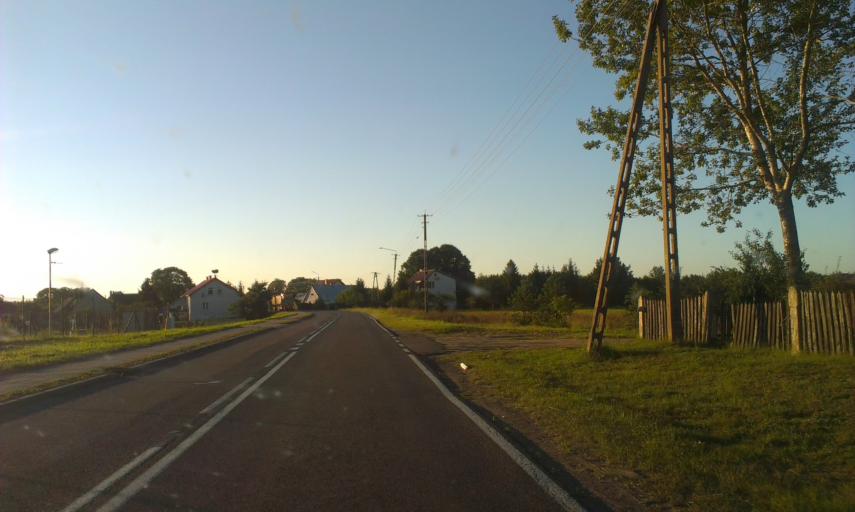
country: PL
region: Pomeranian Voivodeship
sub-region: Powiat czluchowski
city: Czarne
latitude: 53.7319
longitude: 16.8227
